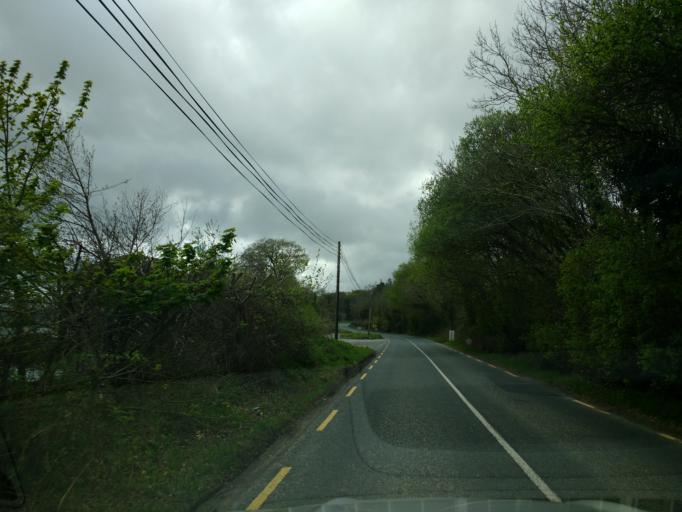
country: IE
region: Ulster
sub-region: County Donegal
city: Ramelton
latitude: 55.0781
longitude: -7.5907
